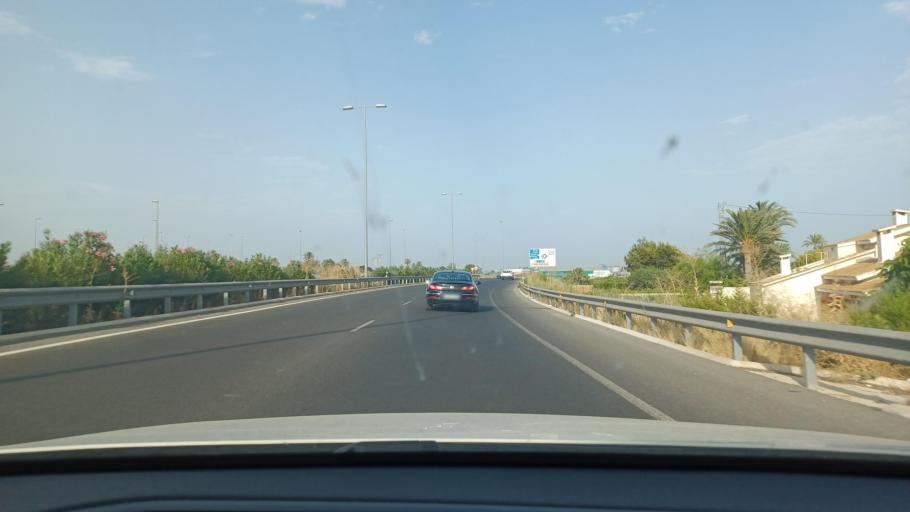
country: ES
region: Valencia
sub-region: Provincia de Alicante
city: Elche
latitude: 38.2623
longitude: -0.6617
